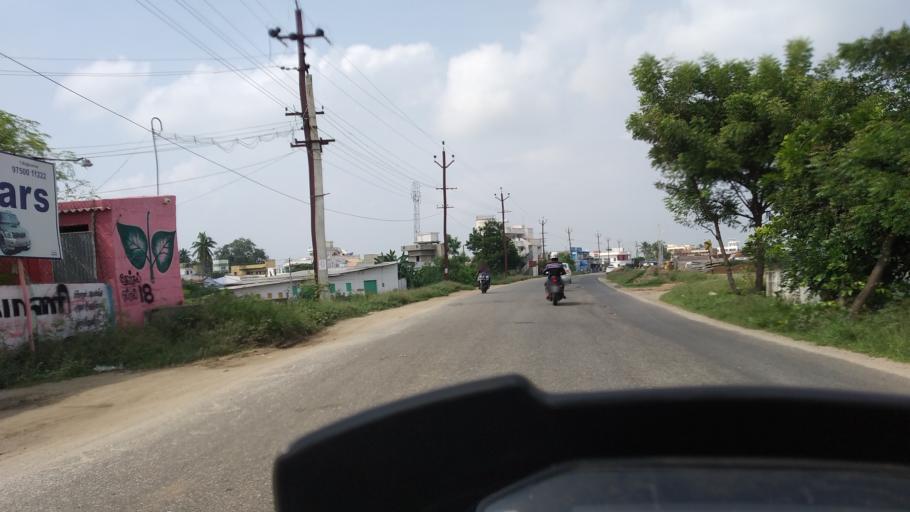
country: IN
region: Tamil Nadu
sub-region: Erode
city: Bhavani
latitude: 11.4385
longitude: 77.7099
